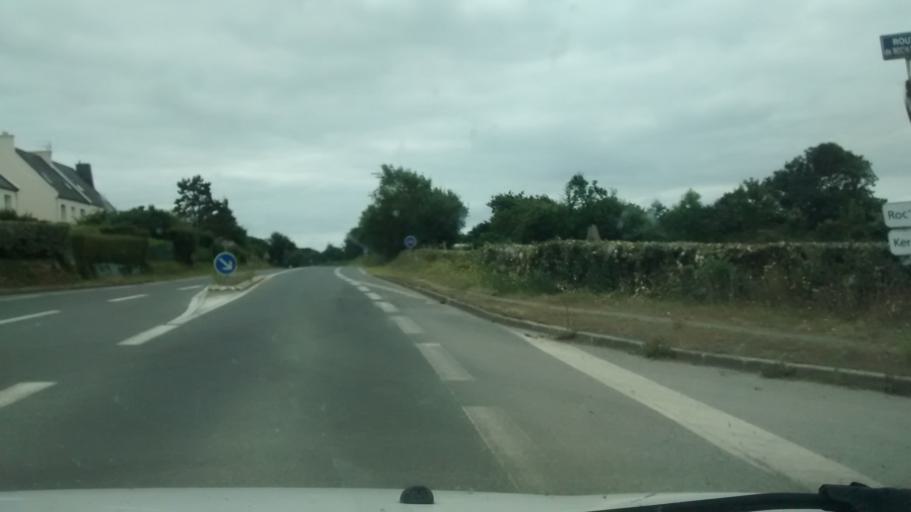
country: FR
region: Brittany
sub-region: Departement du Finistere
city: Plougastel-Daoulas
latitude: 48.3753
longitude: -4.3801
